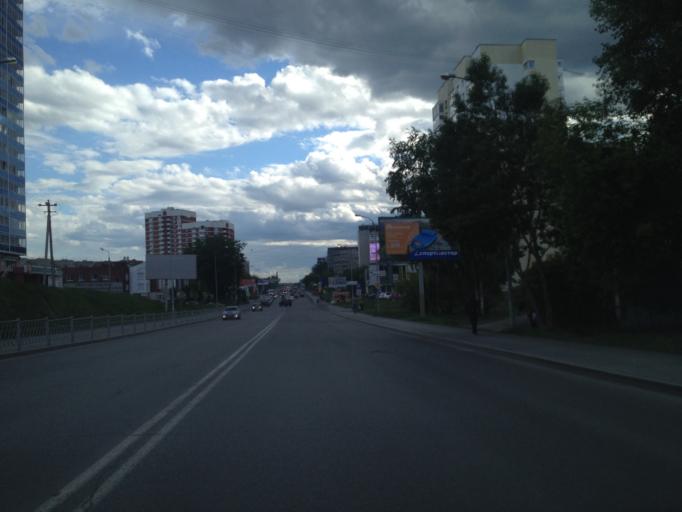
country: RU
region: Sverdlovsk
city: Yekaterinburg
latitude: 56.8548
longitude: 60.5738
